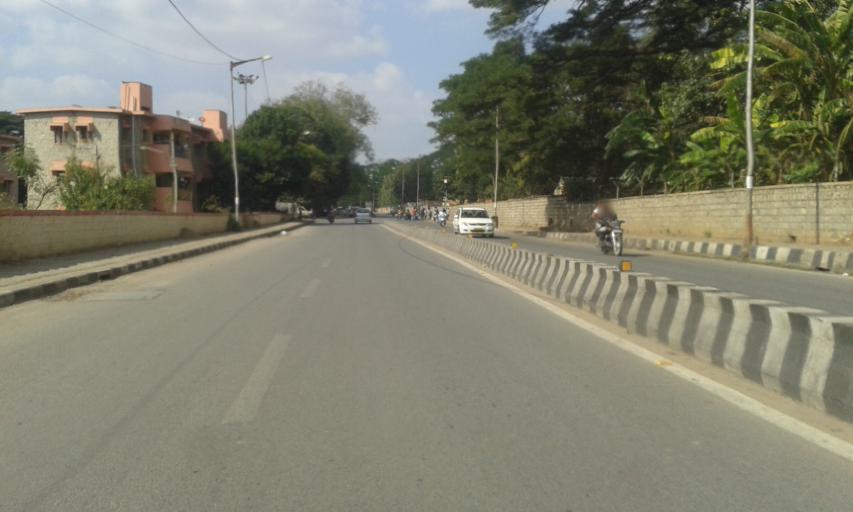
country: IN
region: Karnataka
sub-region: Bangalore Urban
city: Bangalore
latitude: 12.9616
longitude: 77.6193
